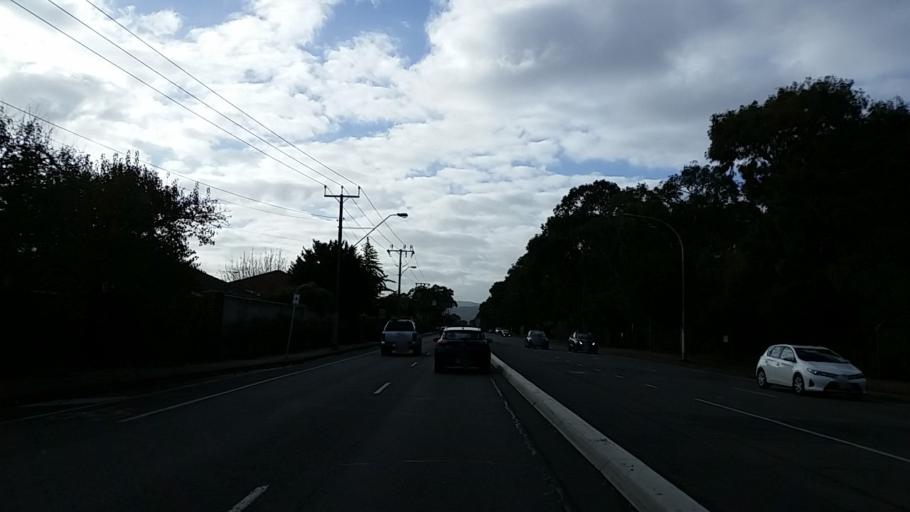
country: AU
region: South Australia
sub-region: Marion
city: Plympton Park
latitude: -34.9958
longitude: 138.5411
